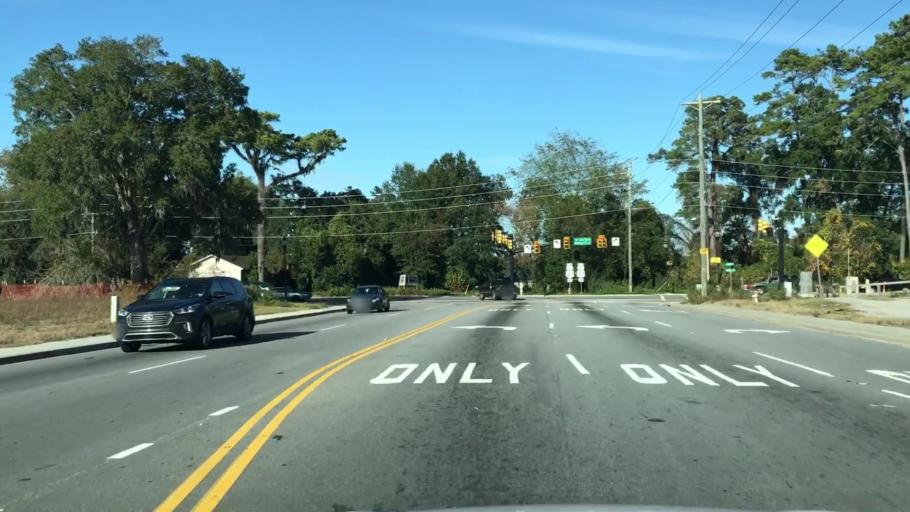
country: US
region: South Carolina
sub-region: Beaufort County
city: Burton
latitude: 32.4411
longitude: -80.7216
